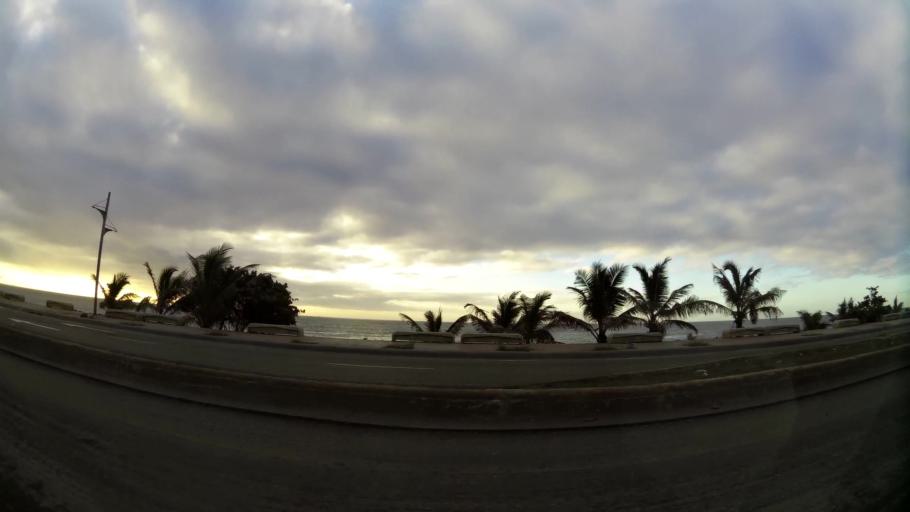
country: DO
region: Nacional
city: Bella Vista
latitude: 18.4438
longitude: -69.9272
